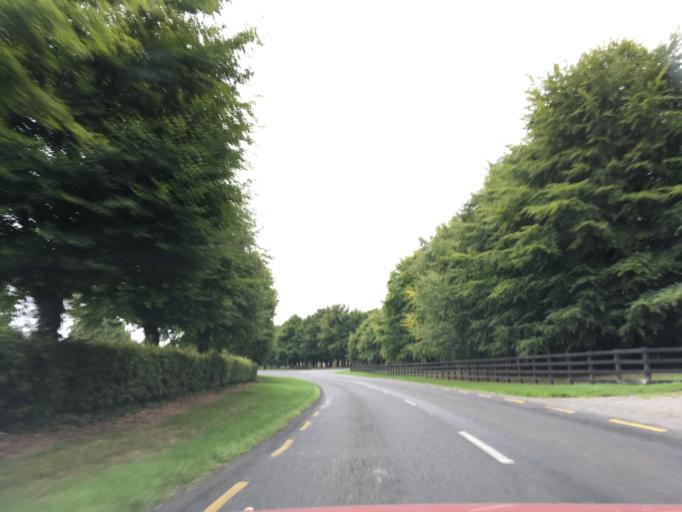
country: IE
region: Munster
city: Cashel
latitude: 52.4626
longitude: -7.8275
